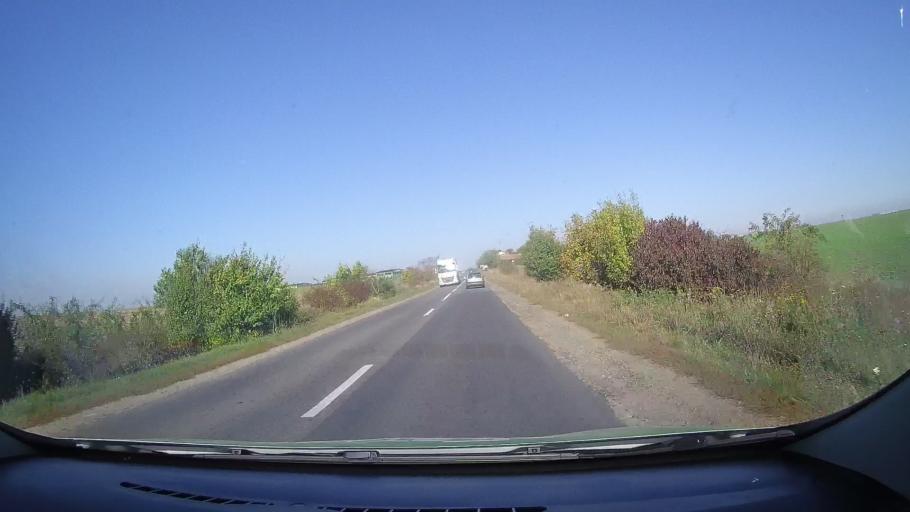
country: RO
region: Satu Mare
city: Carei
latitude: 47.6685
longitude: 22.4870
